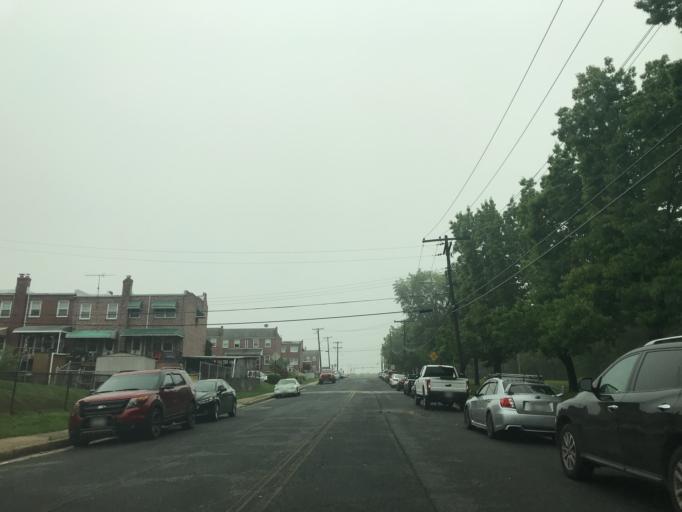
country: US
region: Maryland
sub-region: Baltimore County
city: Rosedale
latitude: 39.2904
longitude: -76.5317
